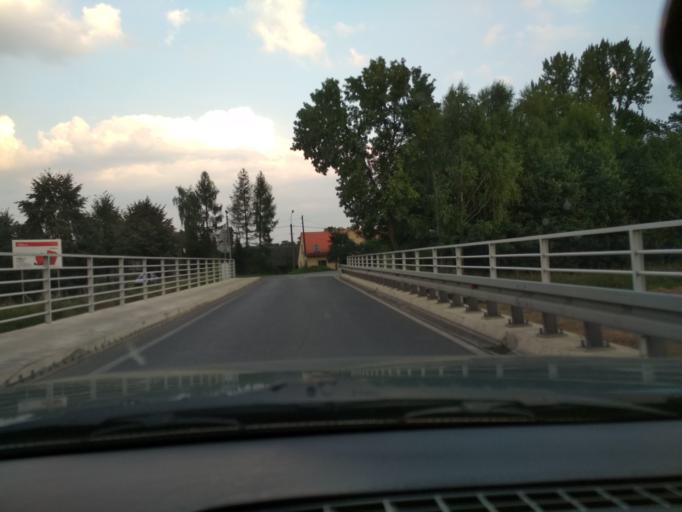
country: PL
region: Silesian Voivodeship
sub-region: Powiat cieszynski
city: Strumien
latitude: 49.9130
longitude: 18.7676
